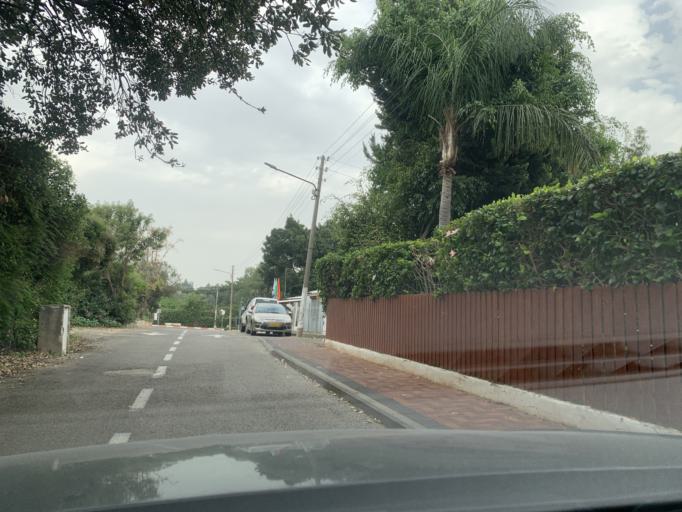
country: IL
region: Central District
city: Kfar Saba
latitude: 32.1929
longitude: 34.9079
